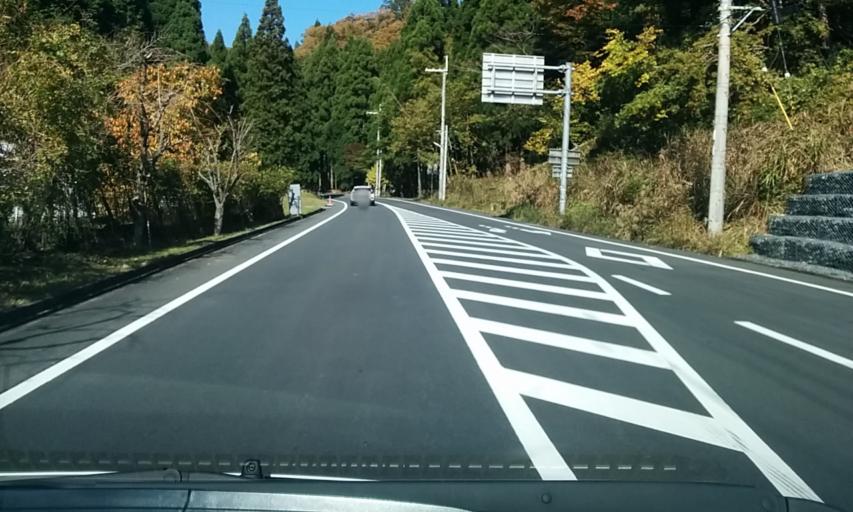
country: JP
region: Kyoto
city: Kameoka
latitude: 35.2112
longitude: 135.5708
